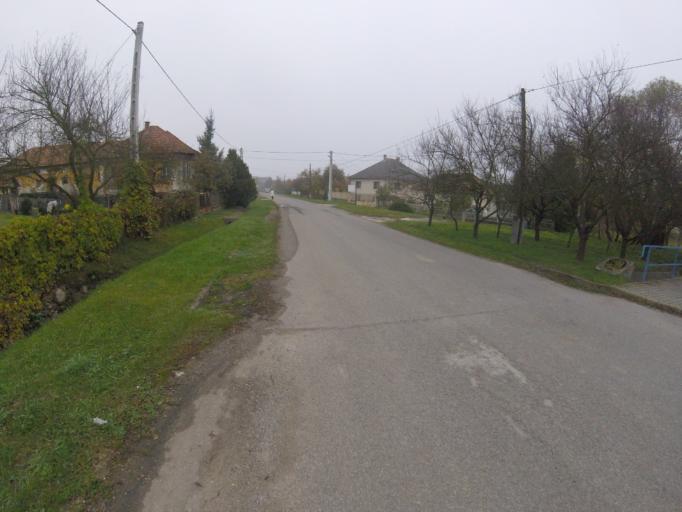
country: HU
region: Heves
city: Szilvasvarad
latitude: 48.1869
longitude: 20.4797
